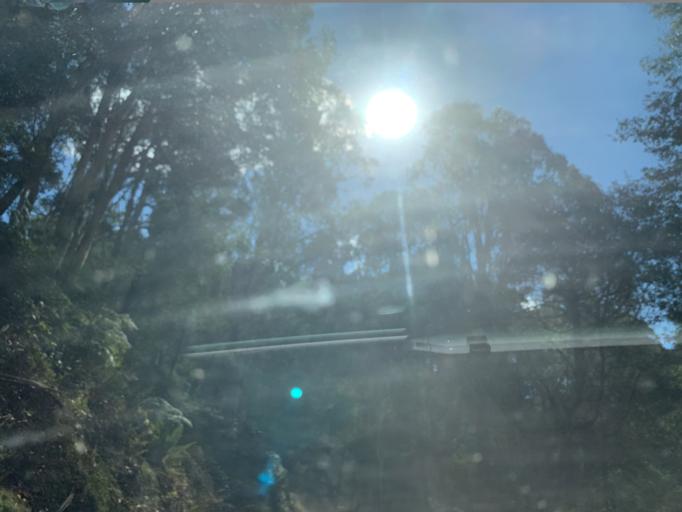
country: AU
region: Victoria
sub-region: Mansfield
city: Mansfield
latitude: -37.1052
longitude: 146.5009
